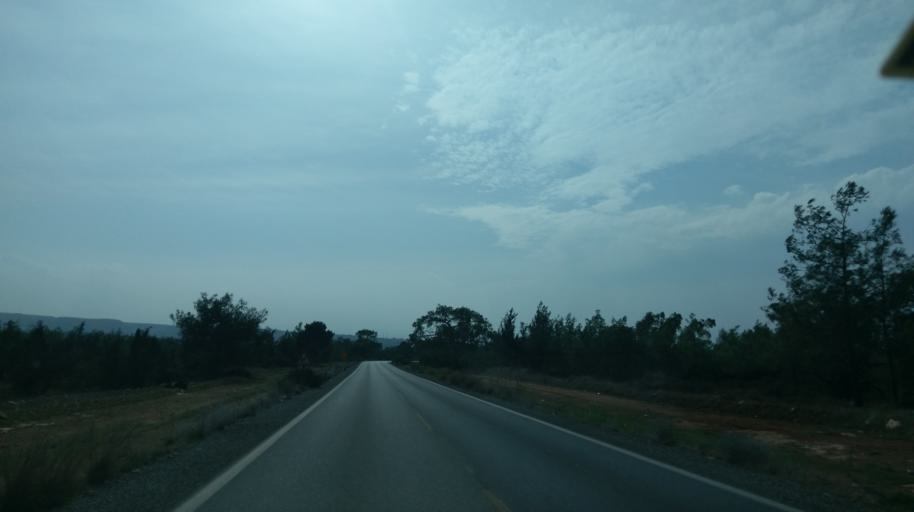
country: CY
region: Lefkosia
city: Morfou
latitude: 35.2754
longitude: 33.0411
